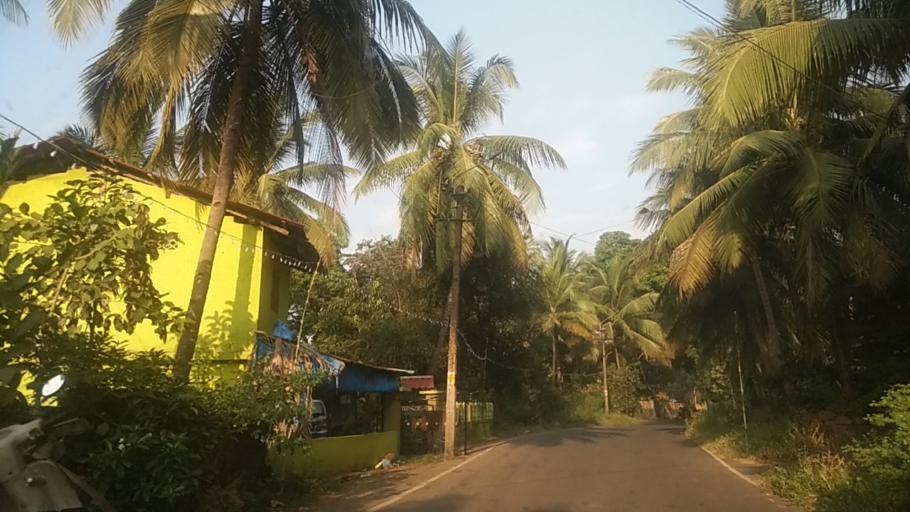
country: IN
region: Goa
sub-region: South Goa
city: Chinchinim
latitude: 15.2322
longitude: 73.9923
